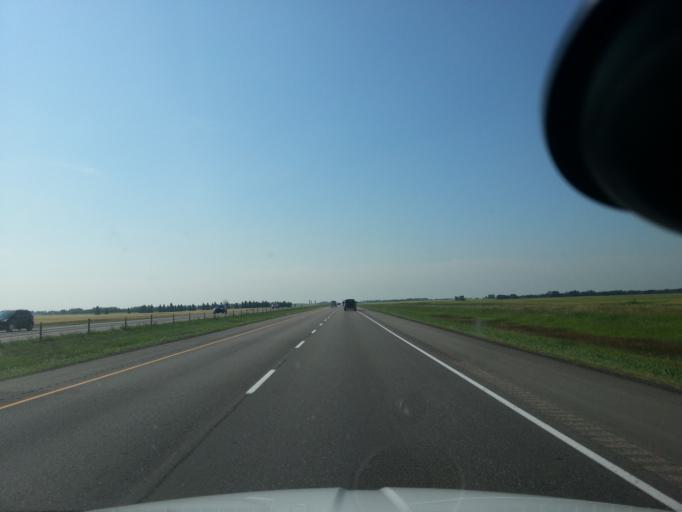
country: CA
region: Alberta
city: Olds
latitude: 51.7597
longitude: -114.0257
